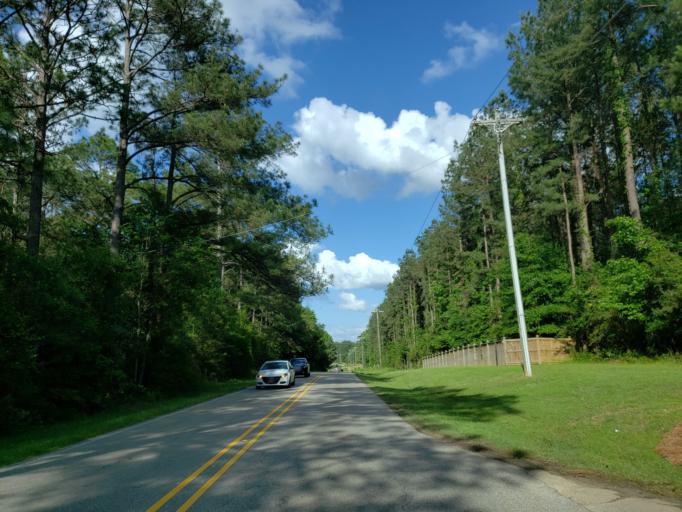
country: US
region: Mississippi
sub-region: Lamar County
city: West Hattiesburg
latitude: 31.2868
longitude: -89.4630
